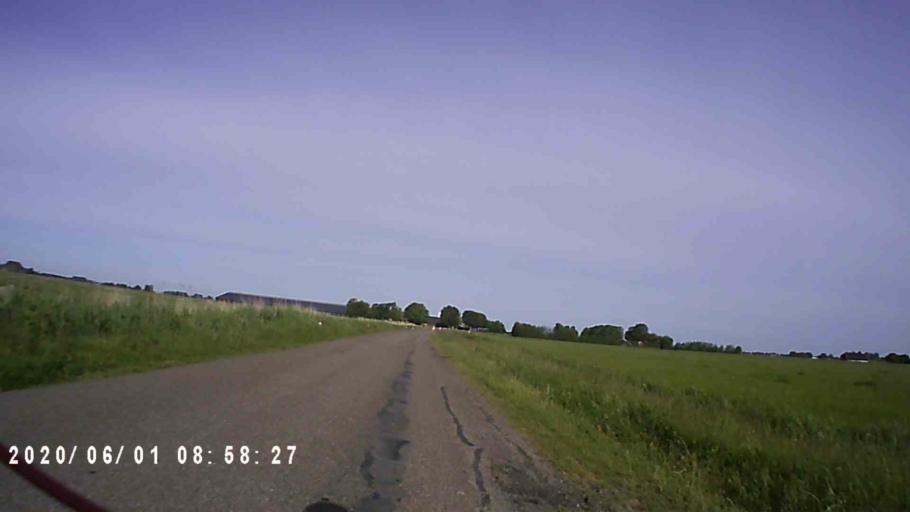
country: NL
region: Friesland
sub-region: Gemeente Ferwerderadiel
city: Hallum
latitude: 53.2817
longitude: 5.8054
